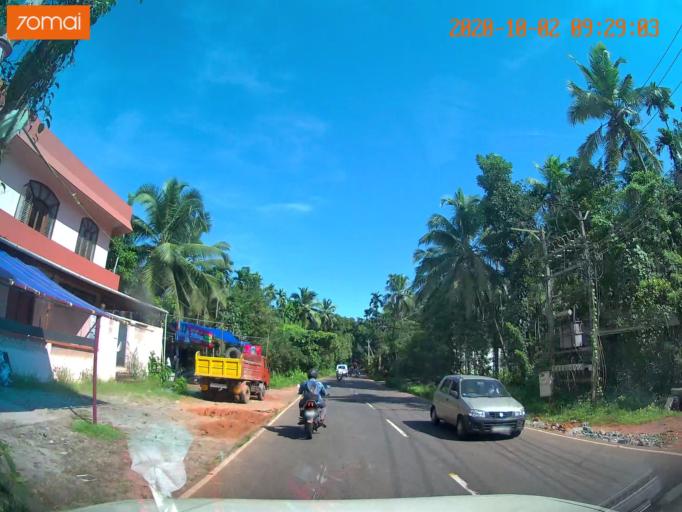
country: IN
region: Kerala
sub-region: Kozhikode
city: Naduvannur
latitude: 11.6111
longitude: 75.7605
